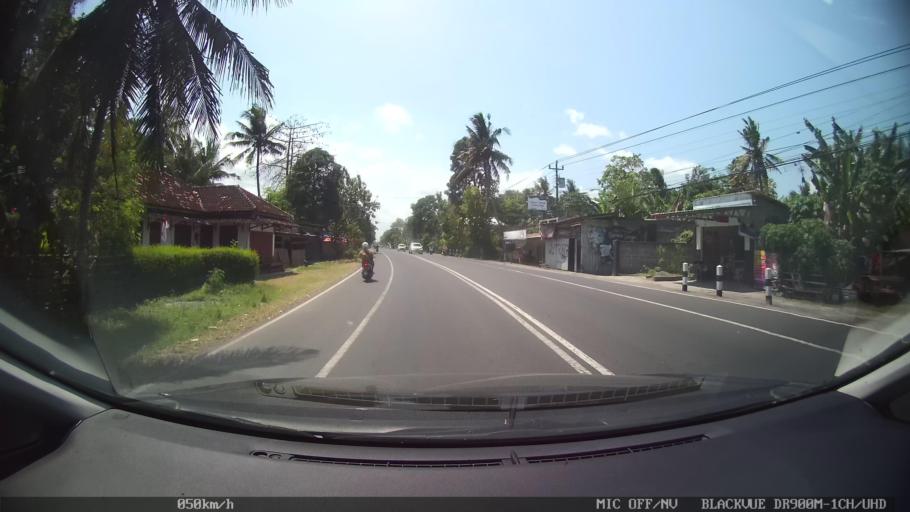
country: ID
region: Daerah Istimewa Yogyakarta
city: Srandakan
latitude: -7.9382
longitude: 110.2563
